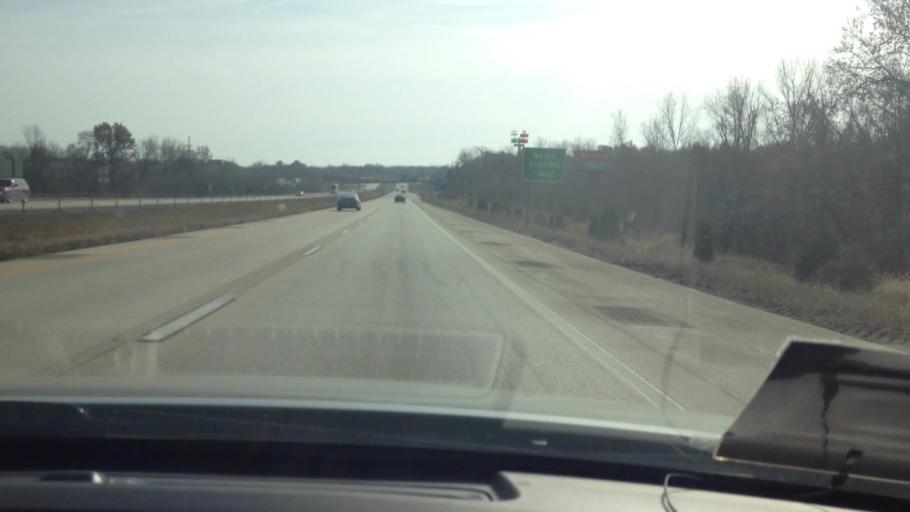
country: US
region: Missouri
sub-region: Cass County
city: Harrisonville
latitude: 38.6425
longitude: -94.3593
